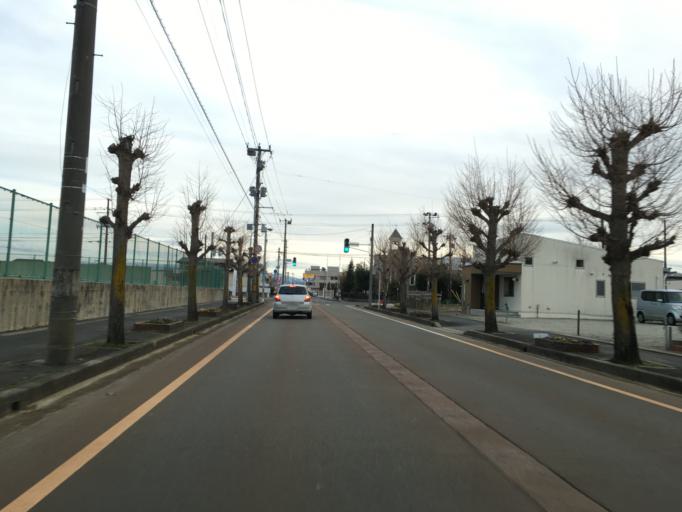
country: JP
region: Yamagata
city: Nagai
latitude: 38.0963
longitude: 140.0364
